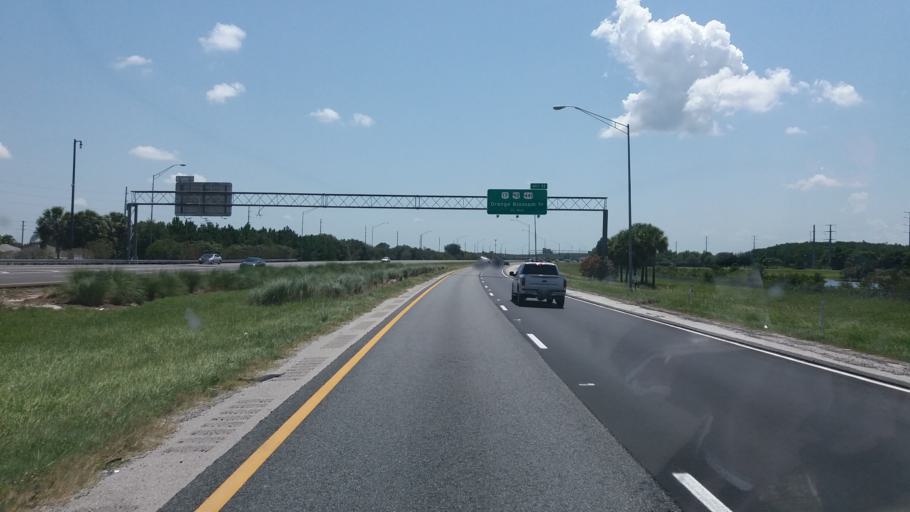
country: US
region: Florida
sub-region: Orange County
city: Hunters Creek
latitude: 28.3751
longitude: -81.4191
